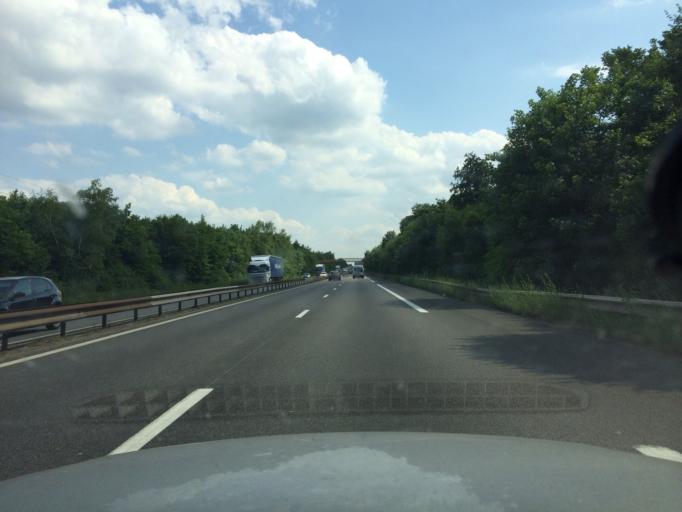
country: FR
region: Lorraine
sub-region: Departement de Meurthe-et-Moselle
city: Laxou
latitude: 48.6766
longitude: 6.1203
